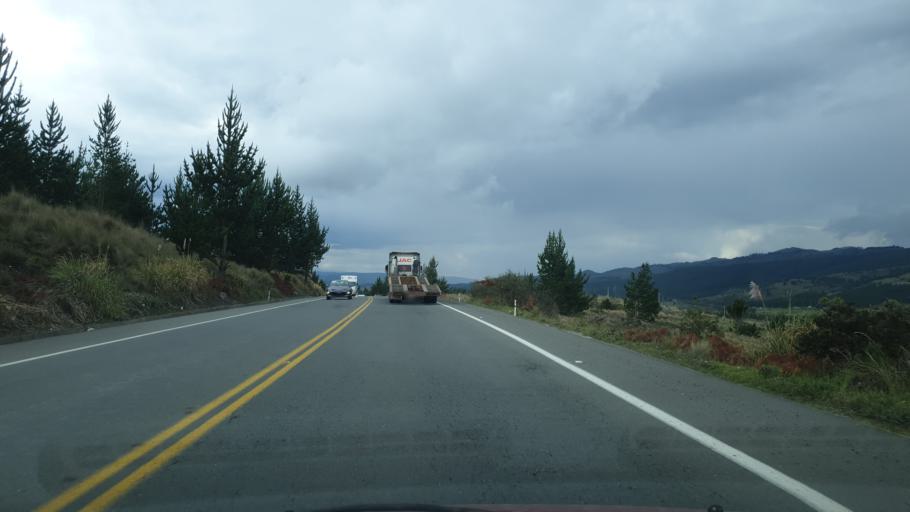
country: EC
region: Chimborazo
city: Alausi
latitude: -2.0401
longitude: -78.7373
